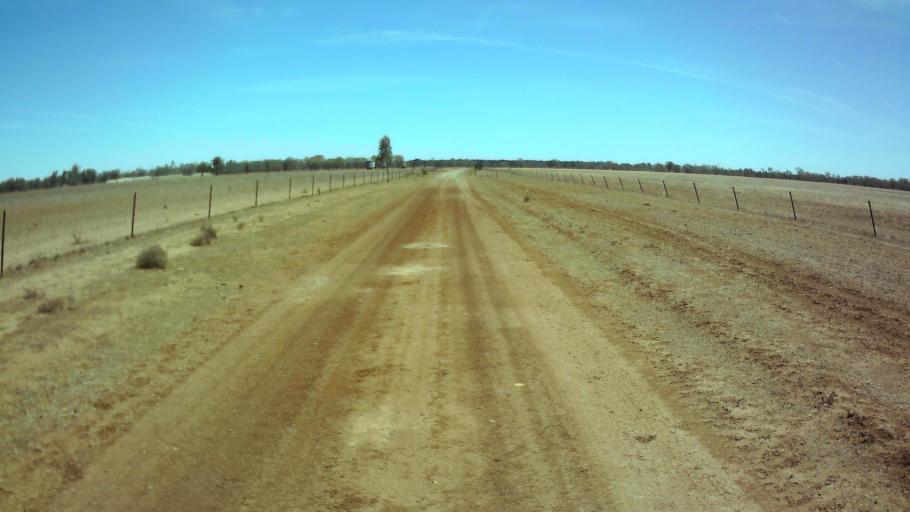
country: AU
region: New South Wales
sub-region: Bland
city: West Wyalong
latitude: -33.8249
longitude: 147.6410
